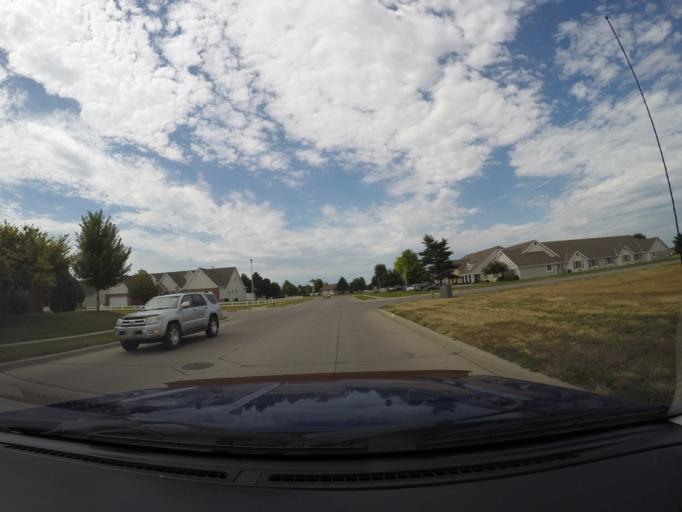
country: US
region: Nebraska
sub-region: Buffalo County
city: Kearney
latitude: 40.7159
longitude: -99.0894
